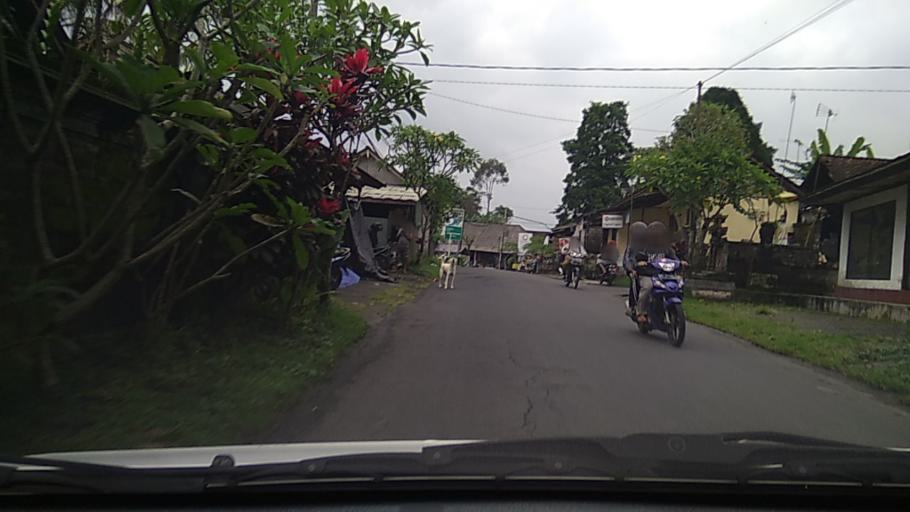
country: ID
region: Bali
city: Banjar Manukayaanyar
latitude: -8.4184
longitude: 115.2992
